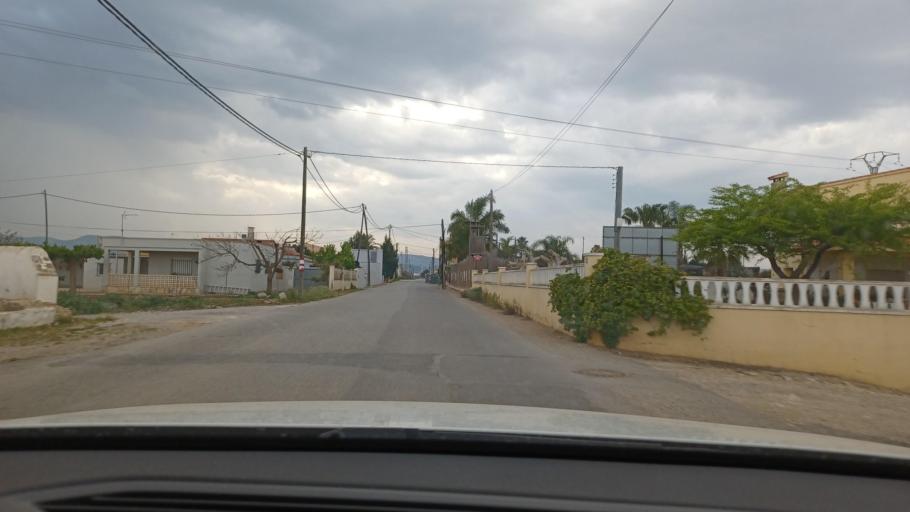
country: ES
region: Valencia
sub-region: Provincia de Castello
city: Benicarlo
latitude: 40.4056
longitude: 0.4032
